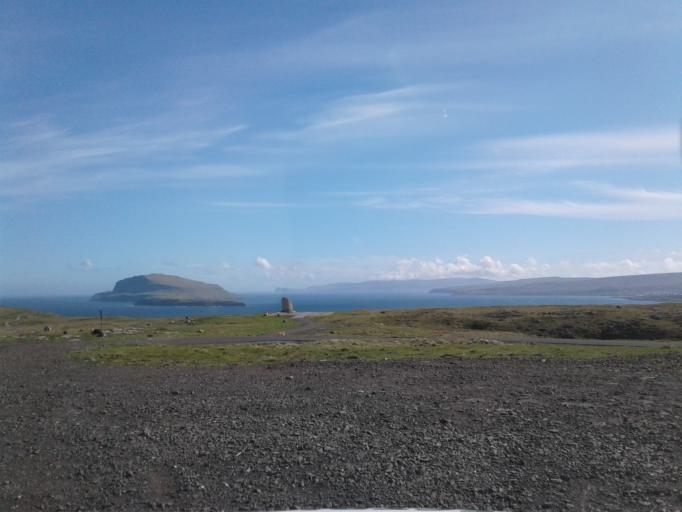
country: FO
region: Streymoy
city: Hoyvik
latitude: 62.0686
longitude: -6.7094
